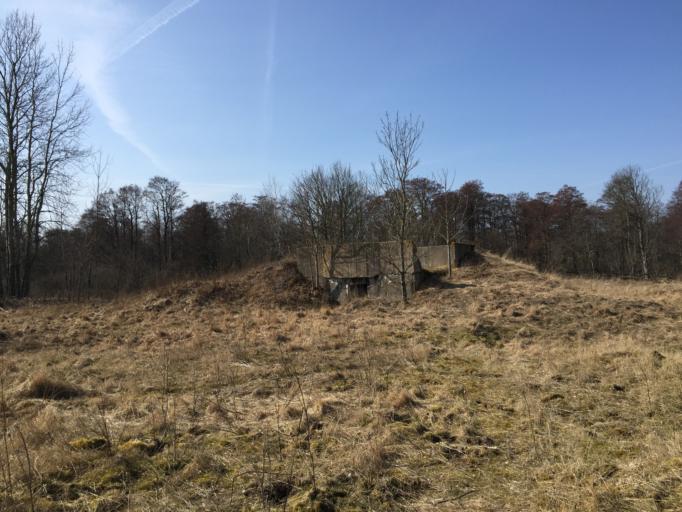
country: LV
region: Dundaga
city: Dundaga
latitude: 57.9242
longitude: 22.0597
